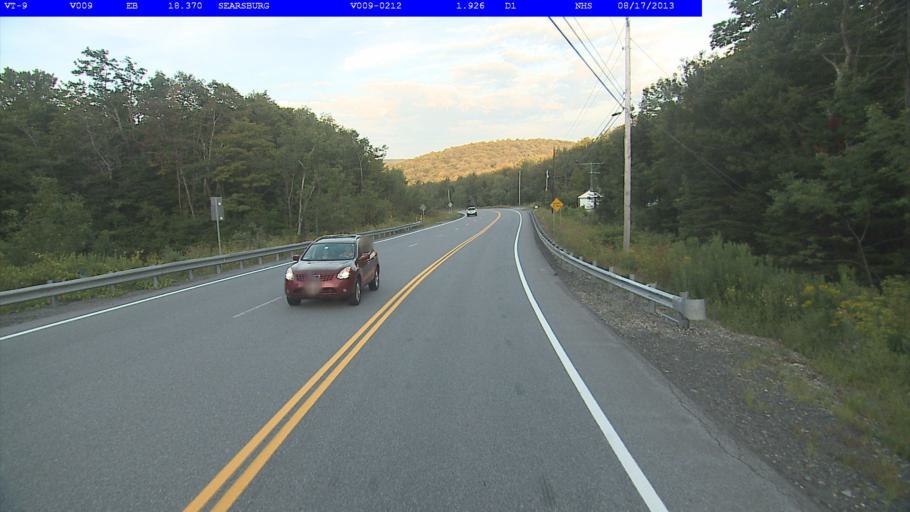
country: US
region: Vermont
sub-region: Windham County
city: Dover
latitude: 42.8950
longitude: -72.9745
